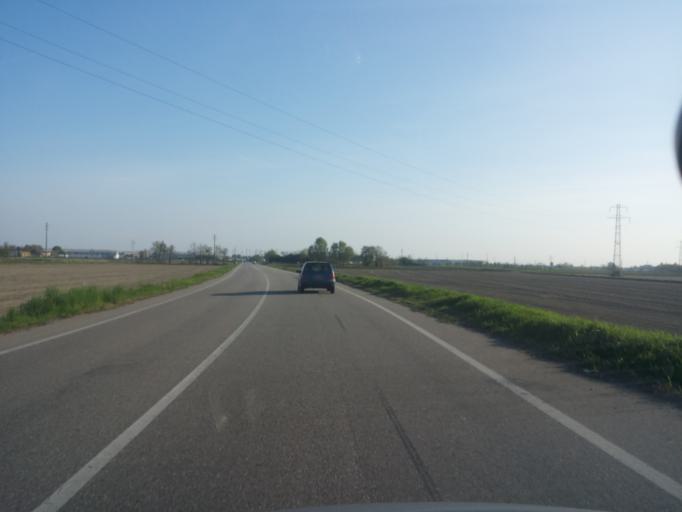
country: IT
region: Lombardy
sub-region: Provincia di Pavia
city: Mortara
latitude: 45.2564
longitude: 8.7145
